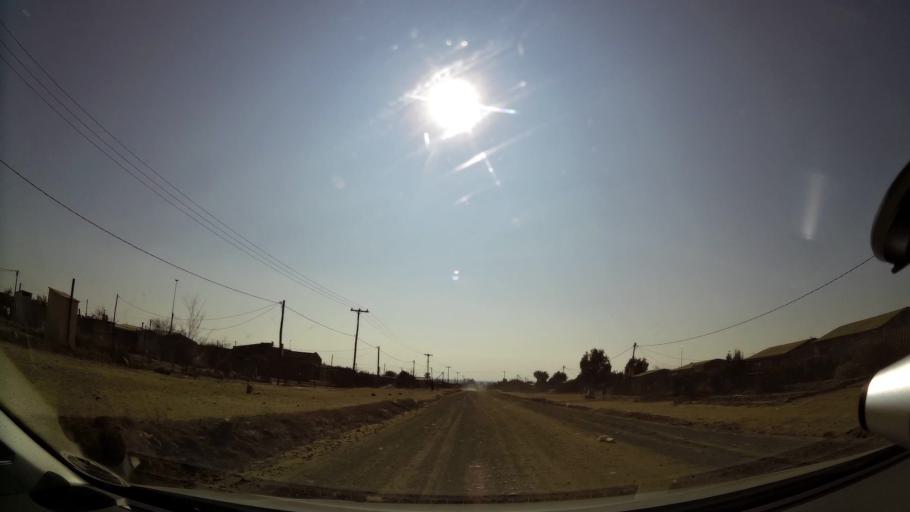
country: ZA
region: Orange Free State
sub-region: Mangaung Metropolitan Municipality
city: Bloemfontein
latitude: -29.1807
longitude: 26.2868
